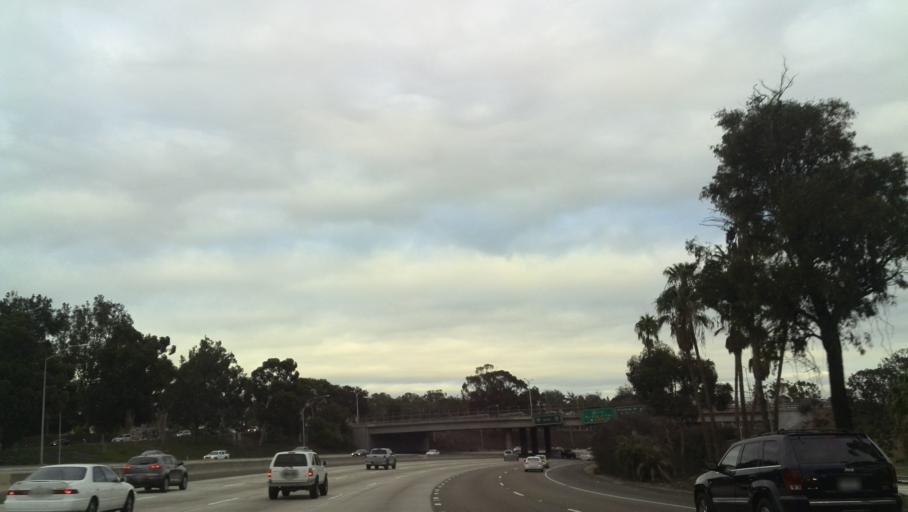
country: US
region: California
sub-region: San Diego County
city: San Diego
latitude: 32.7242
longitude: -117.1536
